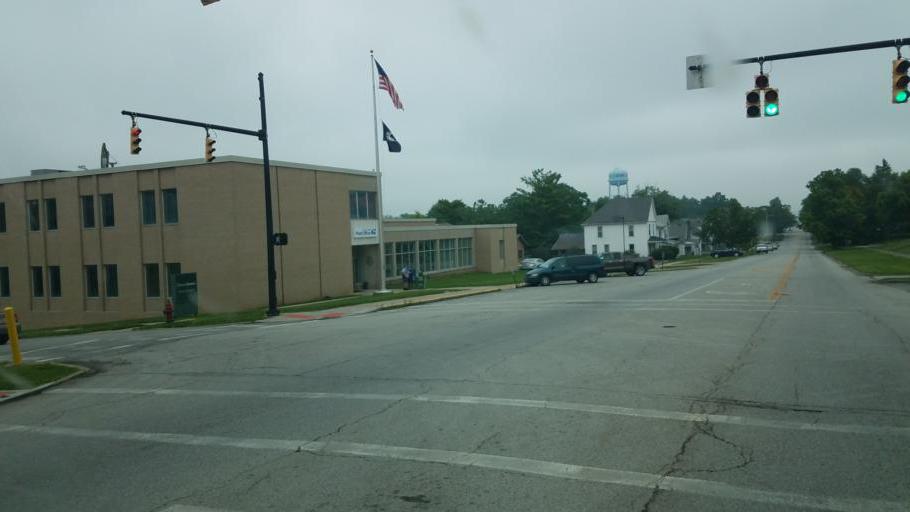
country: US
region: Ohio
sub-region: Highland County
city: Hillsboro
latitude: 39.2047
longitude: -83.6109
